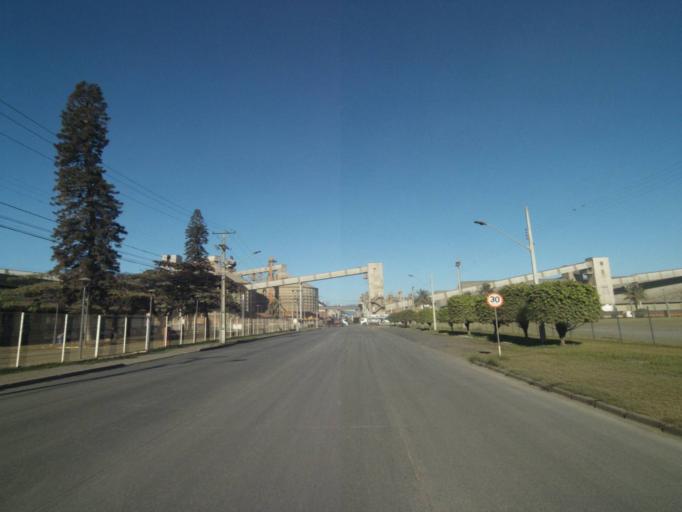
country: BR
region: Parana
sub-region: Paranagua
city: Paranagua
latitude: -25.5054
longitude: -48.5153
